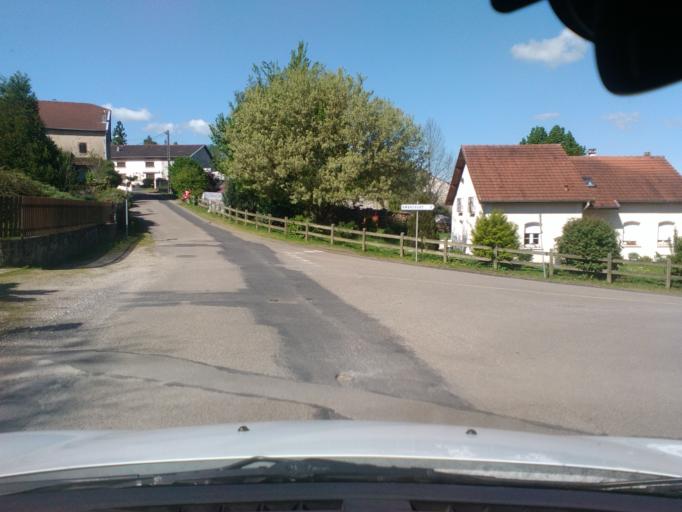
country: FR
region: Lorraine
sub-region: Departement des Vosges
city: Mirecourt
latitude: 48.3230
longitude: 6.1449
